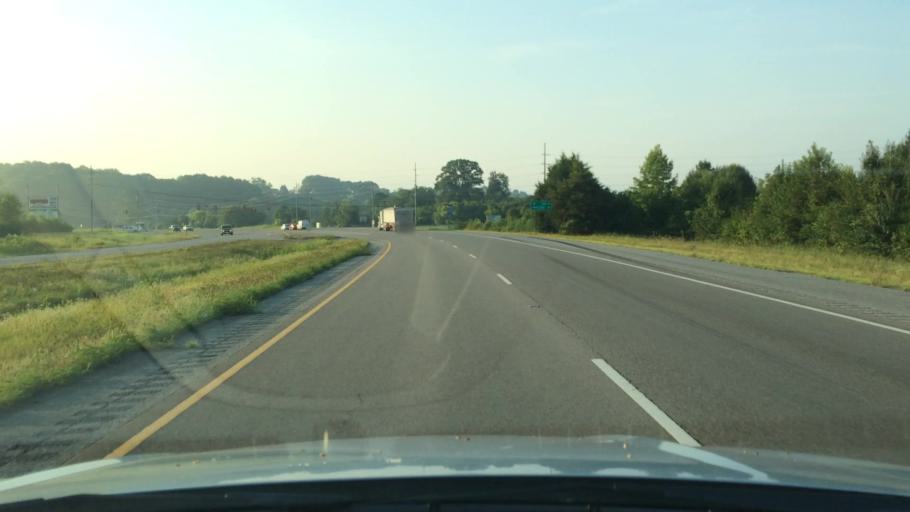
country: US
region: Tennessee
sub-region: Giles County
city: Pulaski
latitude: 35.1723
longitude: -87.0569
